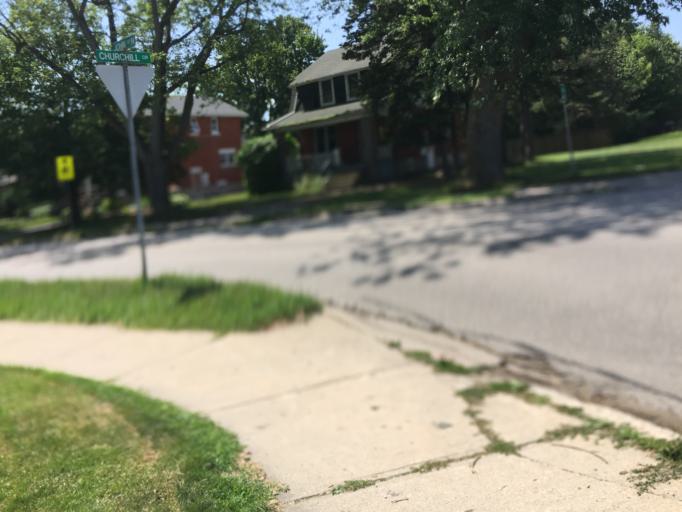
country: CA
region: Ontario
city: Stratford
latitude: 43.3784
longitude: -80.9884
